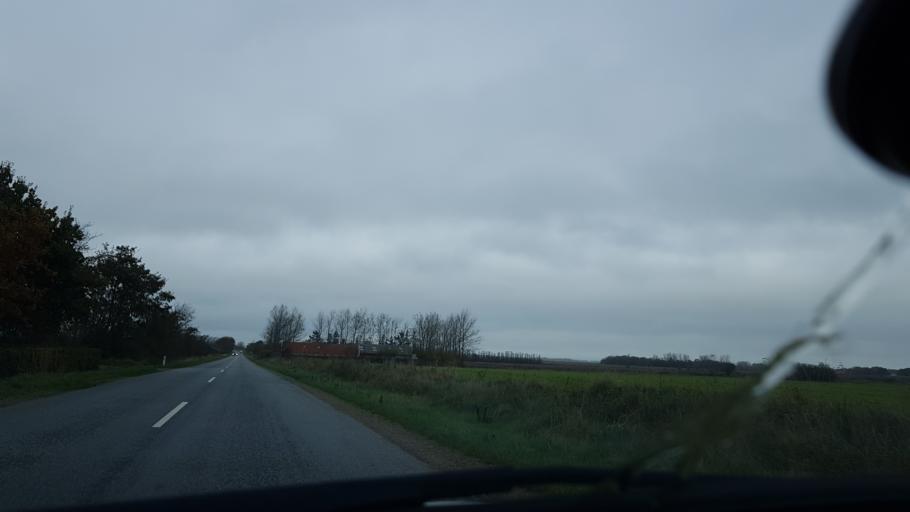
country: DK
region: South Denmark
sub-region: Tonder Kommune
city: Sherrebek
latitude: 55.2313
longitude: 8.8355
